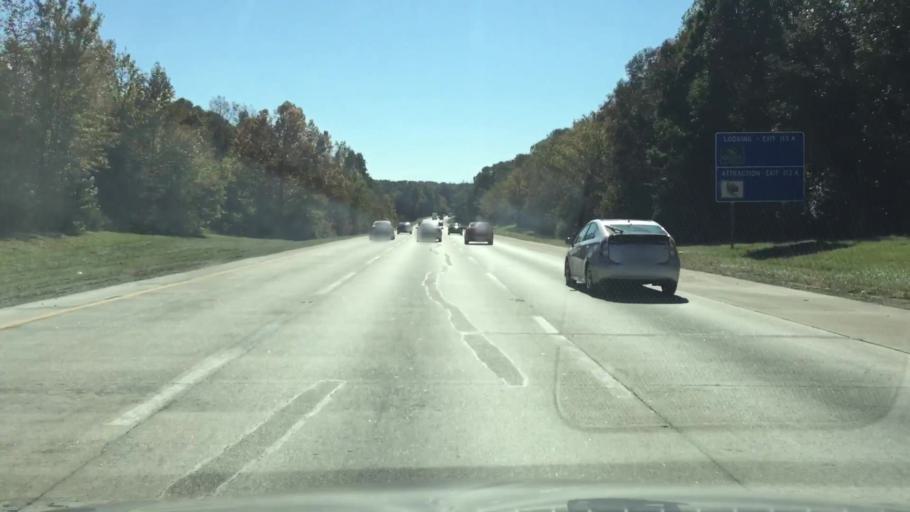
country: US
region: North Carolina
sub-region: Guilford County
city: Jamestown
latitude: 35.9495
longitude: -79.9003
